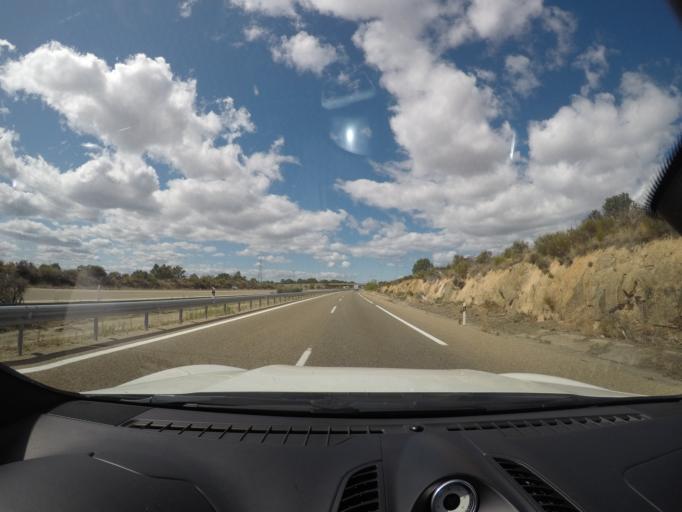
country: ES
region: Castille and Leon
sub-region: Provincia de Zamora
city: Mombuey
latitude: 42.0099
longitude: -6.2863
